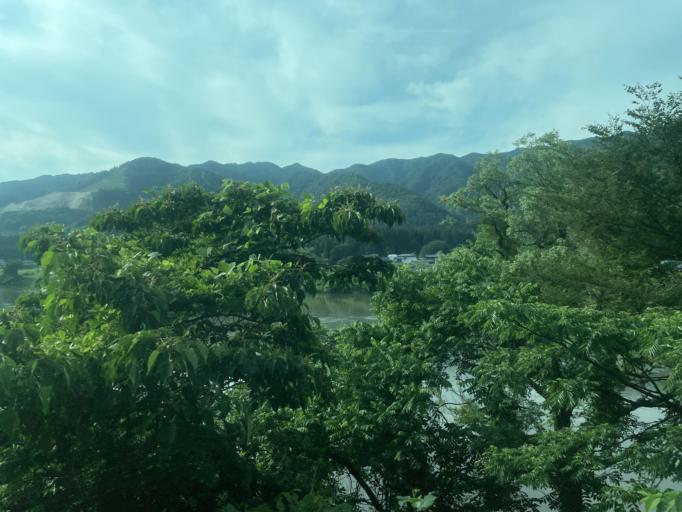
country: JP
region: Niigata
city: Suibara
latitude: 37.7348
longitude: 139.3026
